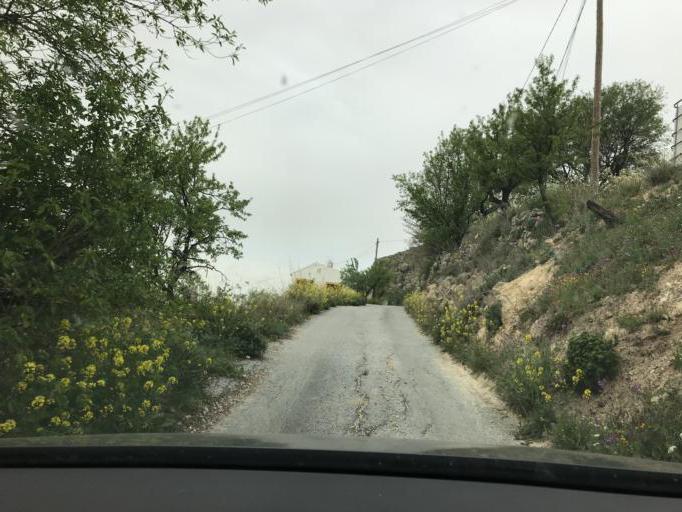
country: ES
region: Andalusia
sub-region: Provincia de Granada
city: Castril
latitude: 37.8026
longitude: -2.7733
